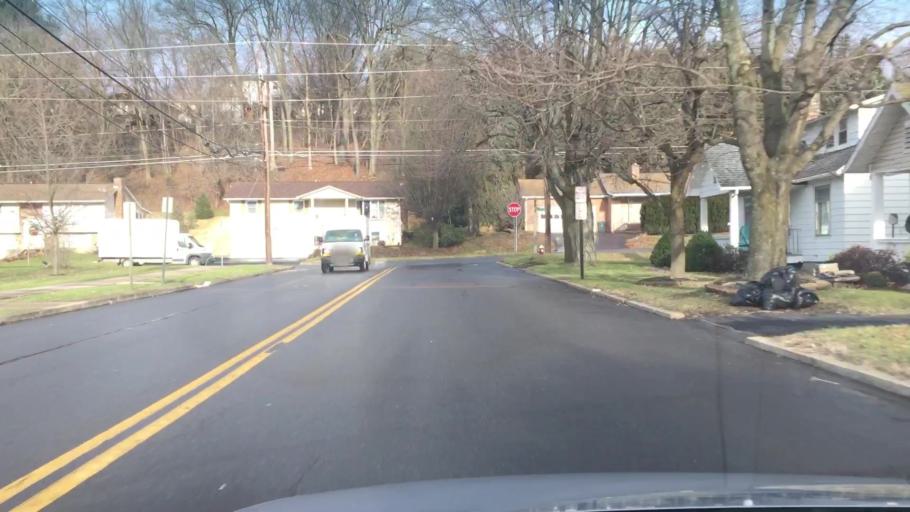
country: US
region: Pennsylvania
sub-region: Columbia County
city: Bloomsburg
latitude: 41.0045
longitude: -76.4426
